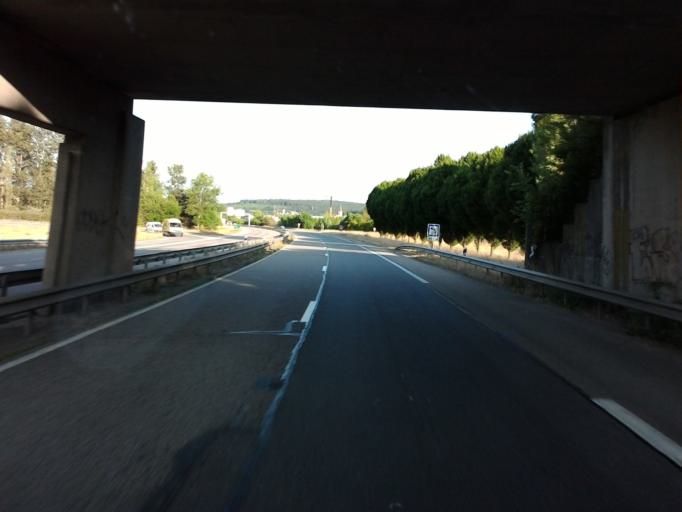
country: FR
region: Lorraine
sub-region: Departement des Vosges
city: Arches
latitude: 48.1255
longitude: 6.5174
